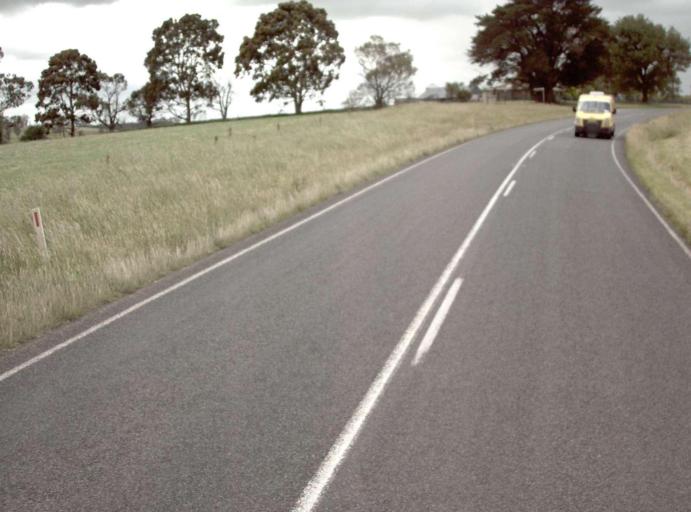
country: AU
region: Victoria
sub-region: Baw Baw
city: Warragul
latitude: -38.1262
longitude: 145.9856
